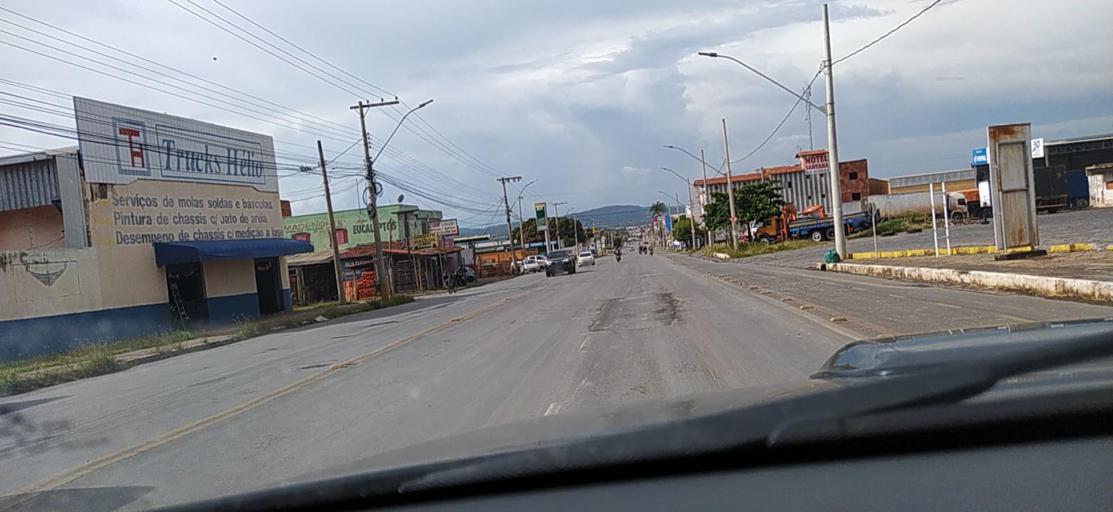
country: BR
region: Minas Gerais
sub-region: Montes Claros
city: Montes Claros
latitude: -16.7410
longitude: -43.8463
